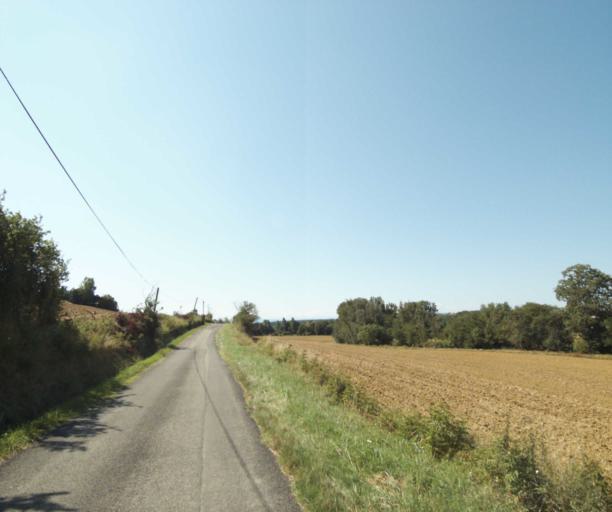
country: FR
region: Midi-Pyrenees
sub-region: Departement de l'Ariege
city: Lezat-sur-Leze
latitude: 43.2671
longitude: 1.3617
